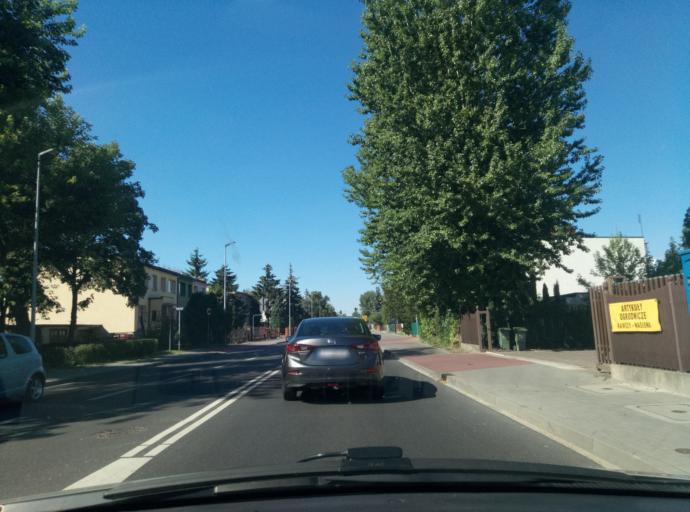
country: PL
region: Kujawsko-Pomorskie
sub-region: Torun
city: Torun
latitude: 53.0269
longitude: 18.6016
